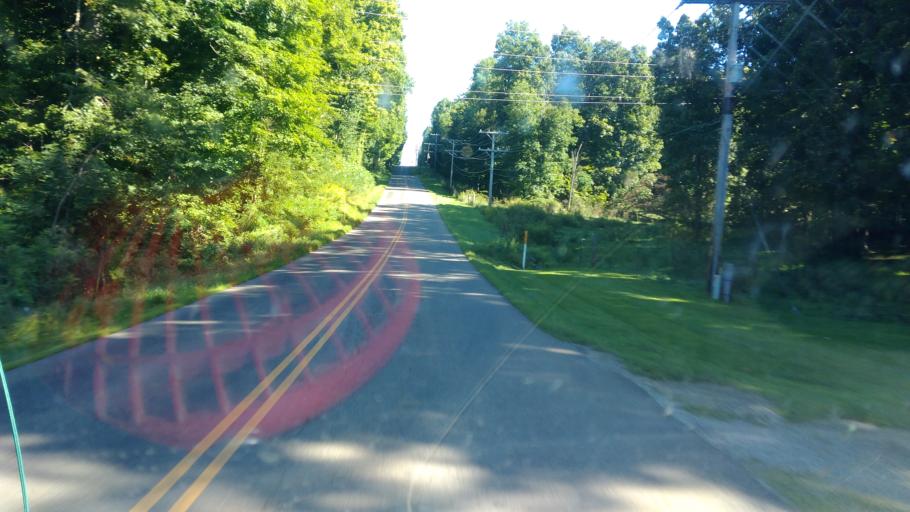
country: US
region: Ohio
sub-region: Knox County
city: Gambier
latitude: 40.4617
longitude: -82.3652
